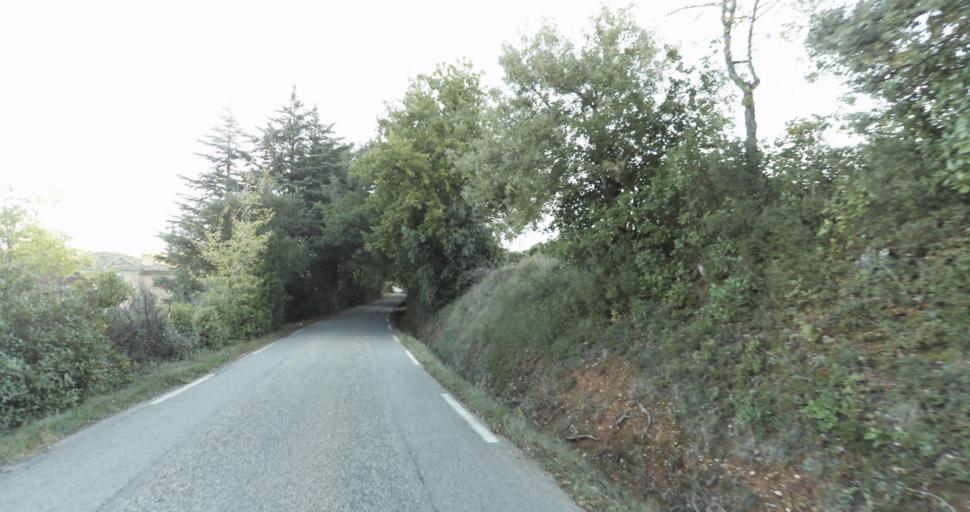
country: FR
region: Provence-Alpes-Cote d'Azur
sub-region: Departement des Bouches-du-Rhone
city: Venelles
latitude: 43.5726
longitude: 5.4829
